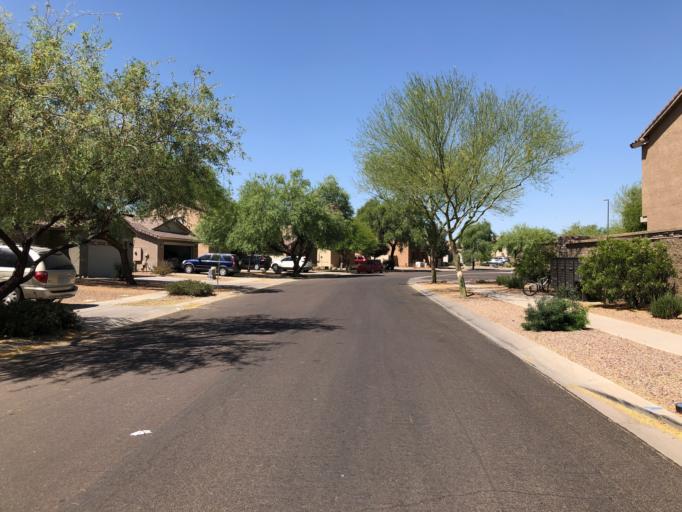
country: US
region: Arizona
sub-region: Maricopa County
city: Queen Creek
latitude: 33.2690
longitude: -111.7019
